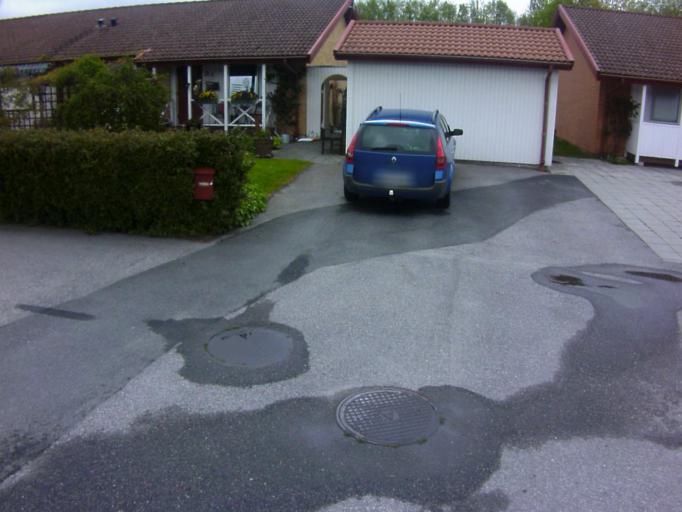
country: SE
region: Blekinge
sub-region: Solvesborgs Kommun
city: Soelvesborg
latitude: 56.0644
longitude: 14.5810
